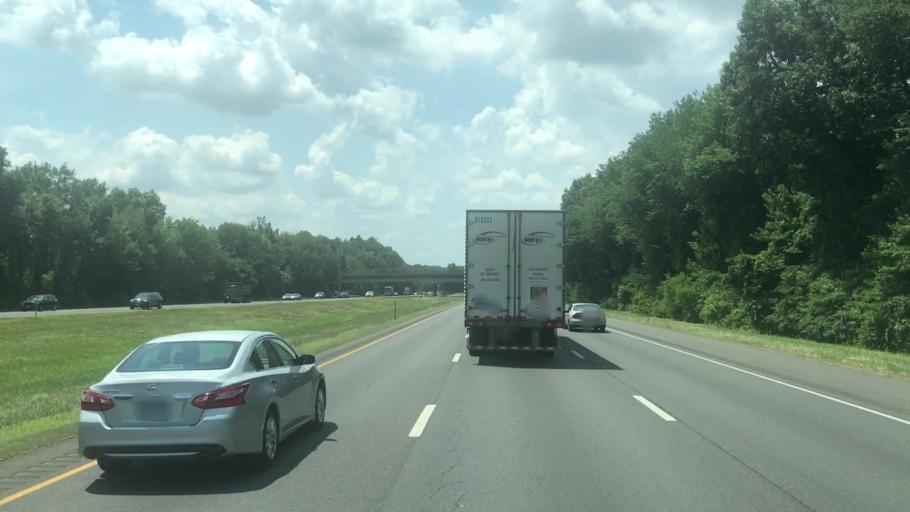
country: US
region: Connecticut
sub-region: Hartford County
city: Plainville
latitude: 41.6485
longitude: -72.8572
